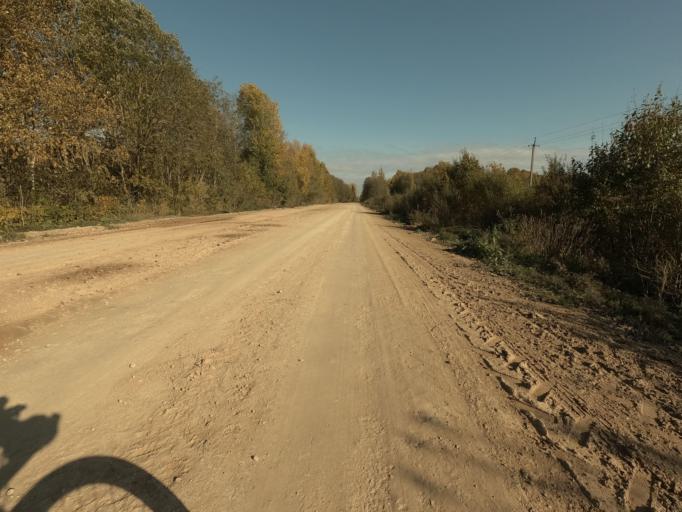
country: RU
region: Novgorod
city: Batetskiy
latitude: 58.8249
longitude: 30.7080
